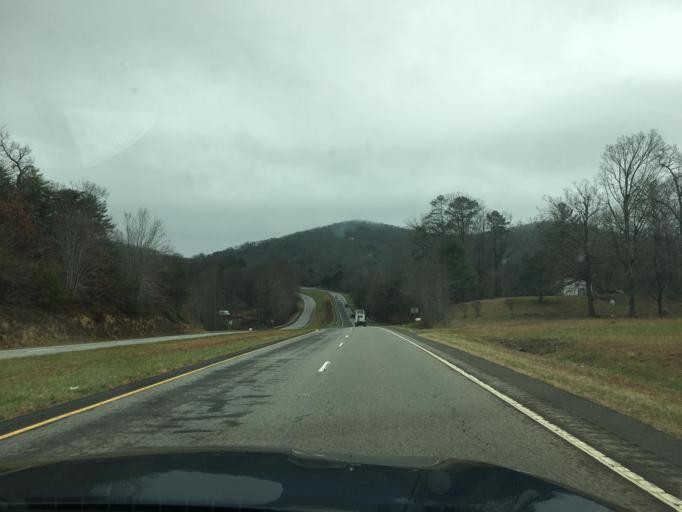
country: US
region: Georgia
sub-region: Fannin County
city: McCaysville
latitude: 35.0137
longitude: -84.3024
